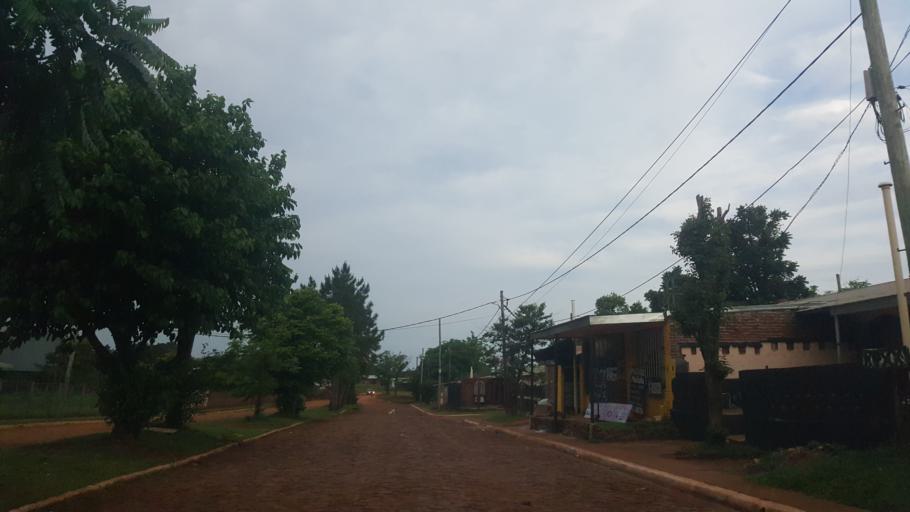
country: AR
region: Misiones
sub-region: Departamento de Candelaria
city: Candelaria
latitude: -27.4766
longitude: -55.7458
